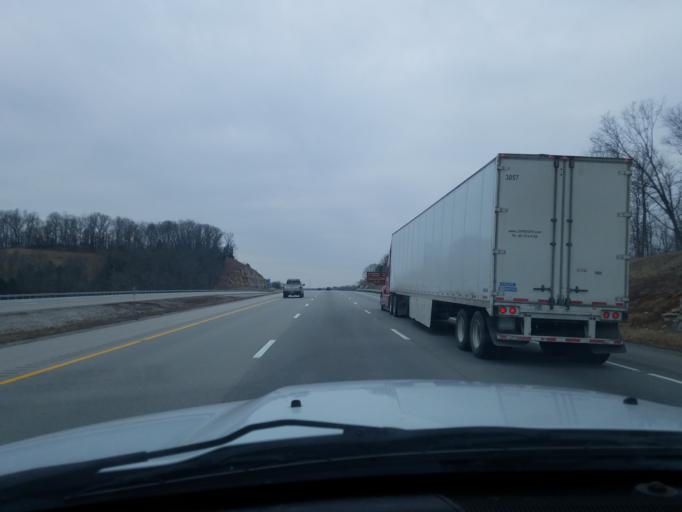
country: US
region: Kentucky
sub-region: Barren County
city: Cave City
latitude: 37.1081
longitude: -86.0388
